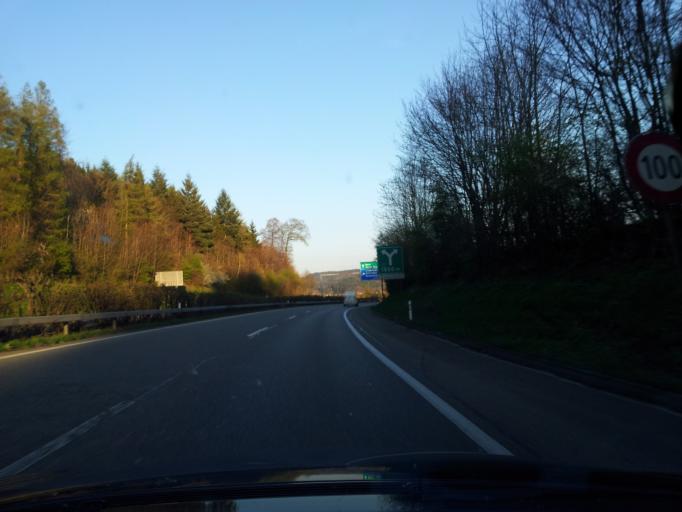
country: CH
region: Bern
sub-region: Bern-Mittelland District
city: Urtenen
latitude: 47.0252
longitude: 7.4822
